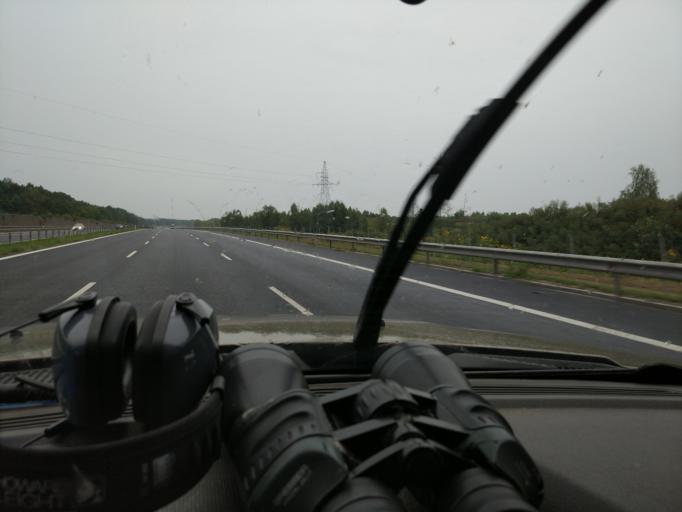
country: PL
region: Masovian Voivodeship
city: Zielonka
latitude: 52.3335
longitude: 21.1572
